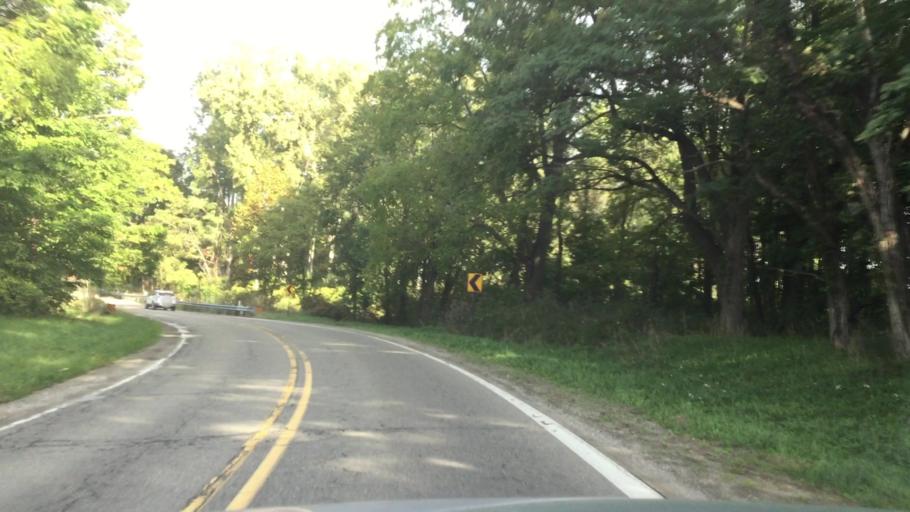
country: US
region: Michigan
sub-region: Livingston County
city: Brighton
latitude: 42.4899
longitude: -83.8531
